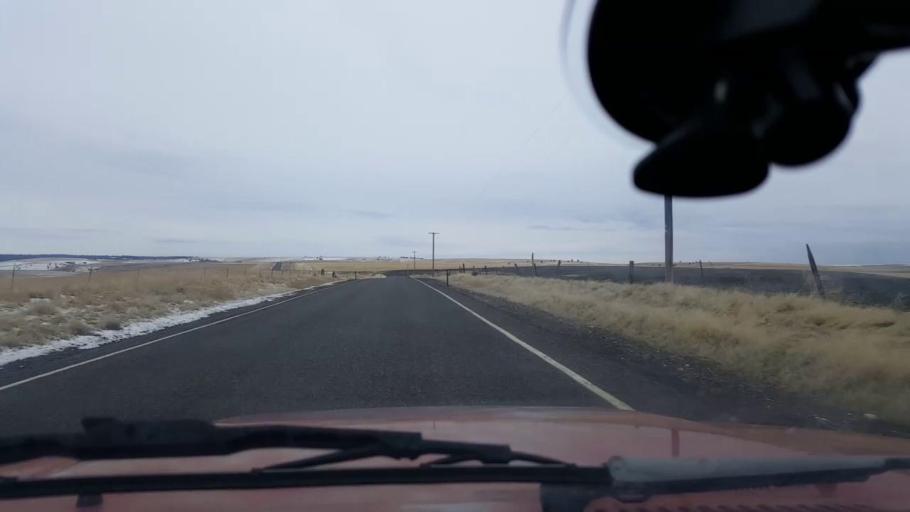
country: US
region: Washington
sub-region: Garfield County
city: Pomeroy
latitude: 46.3238
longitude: -117.3610
